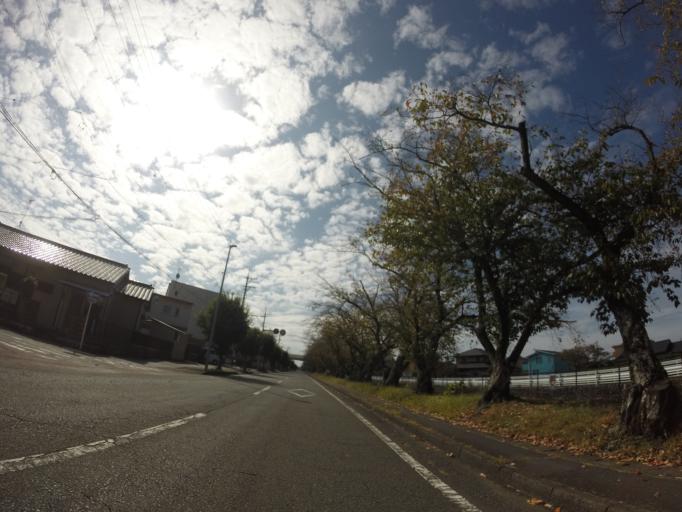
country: JP
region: Shizuoka
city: Yaizu
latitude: 34.8670
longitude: 138.3126
